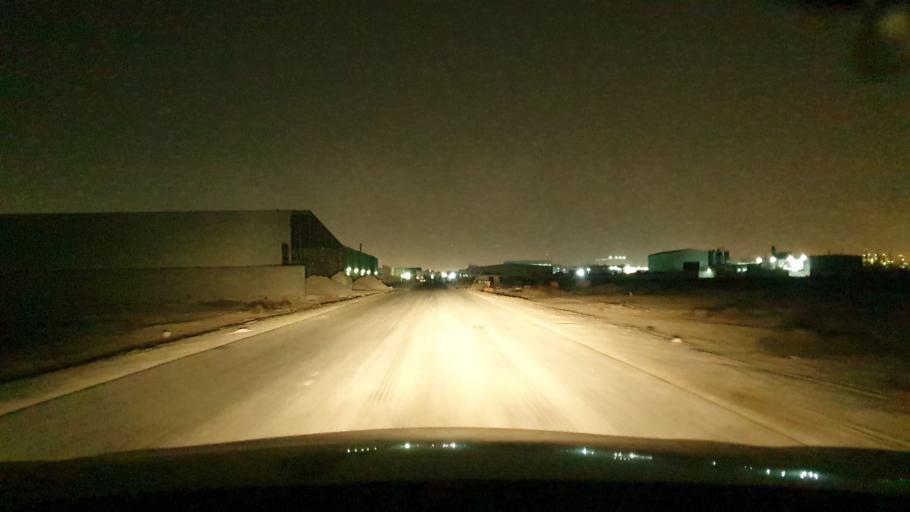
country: BH
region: Northern
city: Sitrah
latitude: 26.0973
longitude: 50.6272
